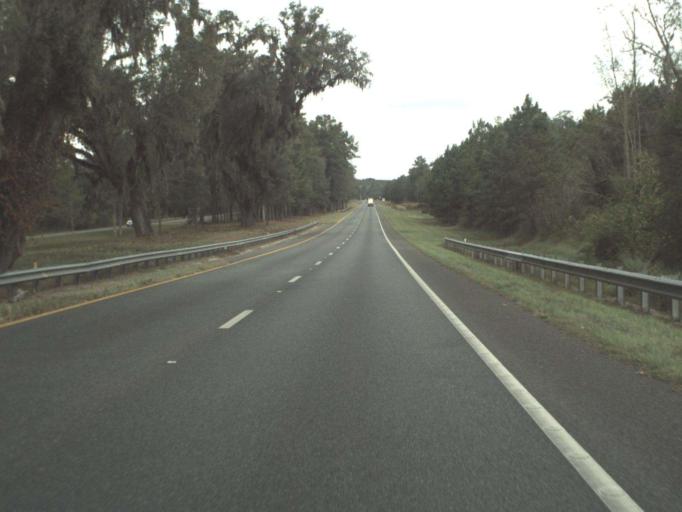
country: US
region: Florida
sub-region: Leon County
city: Tallahassee
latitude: 30.6360
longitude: -84.1687
